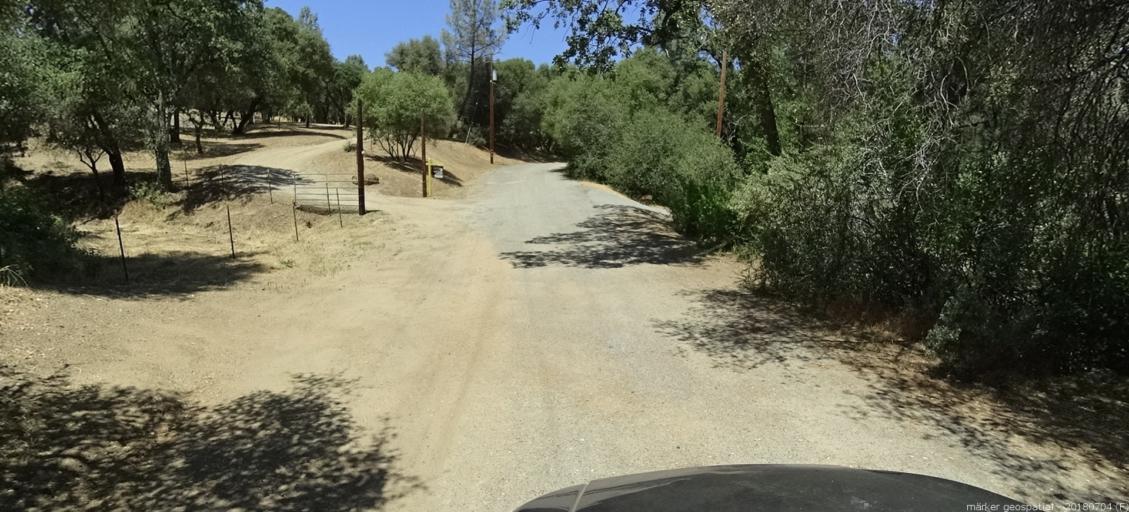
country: US
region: California
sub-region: Fresno County
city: Auberry
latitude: 37.2088
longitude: -119.5523
